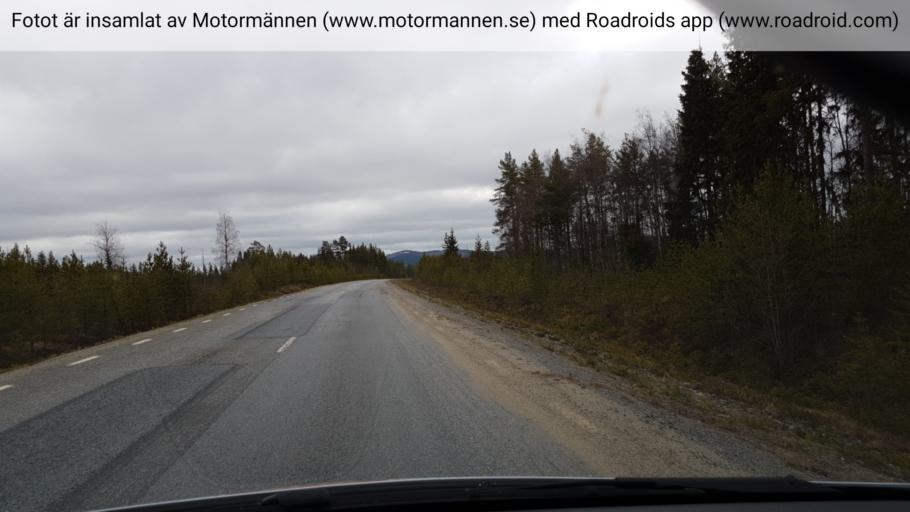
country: SE
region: Vaesterbotten
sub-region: Lycksele Kommun
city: Lycksele
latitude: 63.9851
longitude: 18.4828
